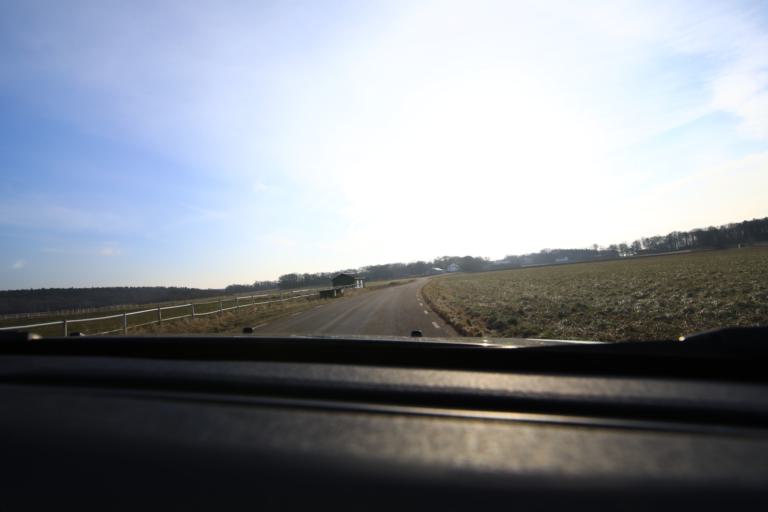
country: SE
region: Halland
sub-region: Varbergs Kommun
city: Varberg
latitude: 57.1983
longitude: 12.2182
